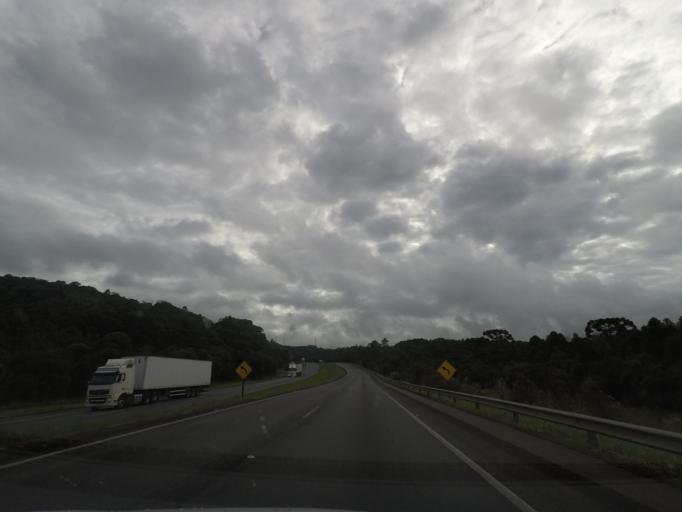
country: BR
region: Parana
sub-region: Campina Grande Do Sul
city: Campina Grande do Sul
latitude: -25.2649
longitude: -48.9155
